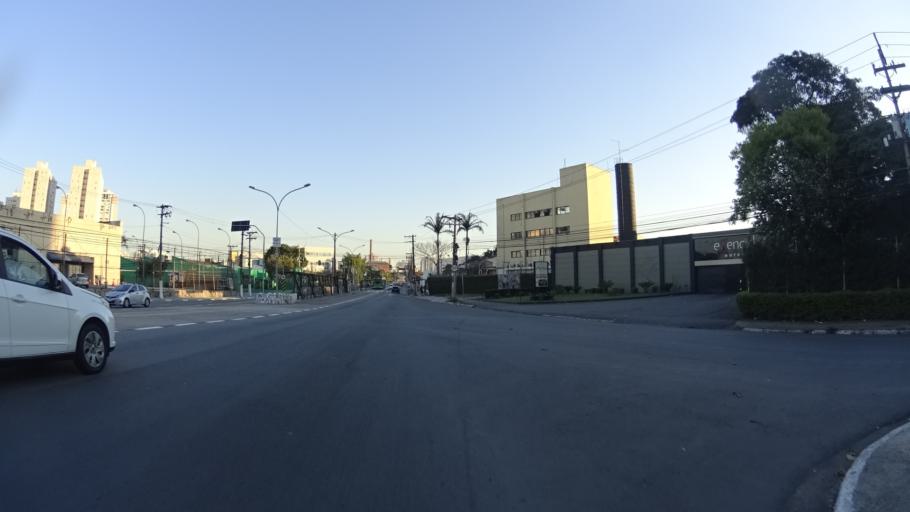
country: BR
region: Sao Paulo
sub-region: Sao Paulo
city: Sao Paulo
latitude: -23.5114
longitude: -46.6903
